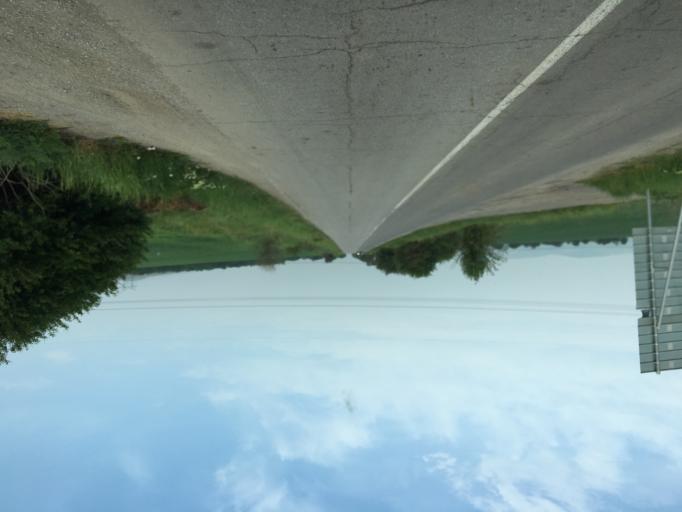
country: BG
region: Kyustendil
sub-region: Obshtina Bobovdol
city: Bobovdol
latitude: 42.4535
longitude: 23.1089
